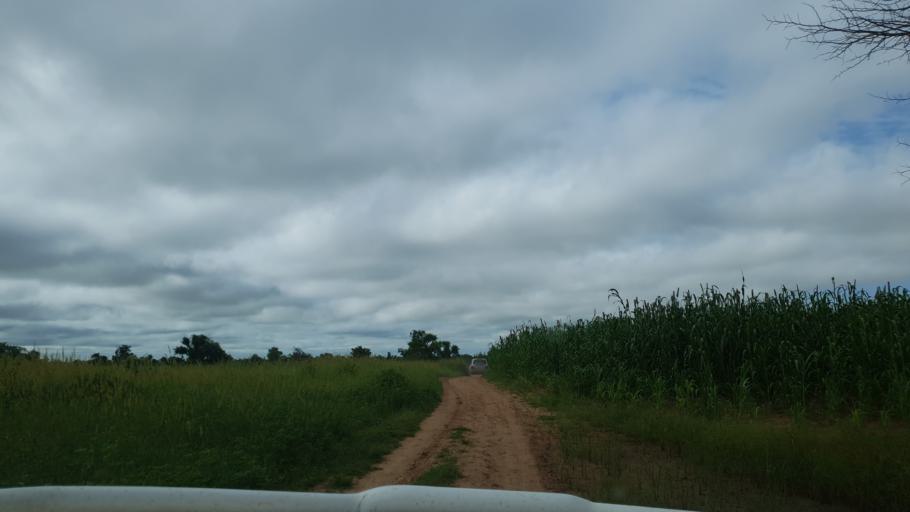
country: ML
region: Segou
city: Baroueli
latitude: 13.4980
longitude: -6.8969
